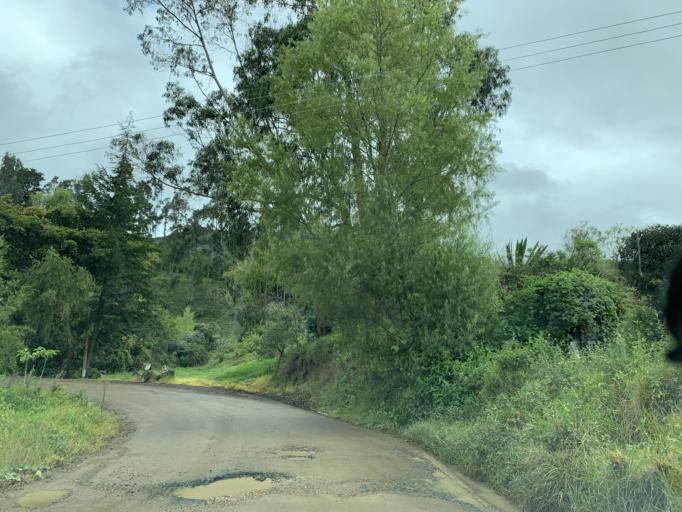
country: CO
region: Boyaca
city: Tibana
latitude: 5.3167
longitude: -73.4211
